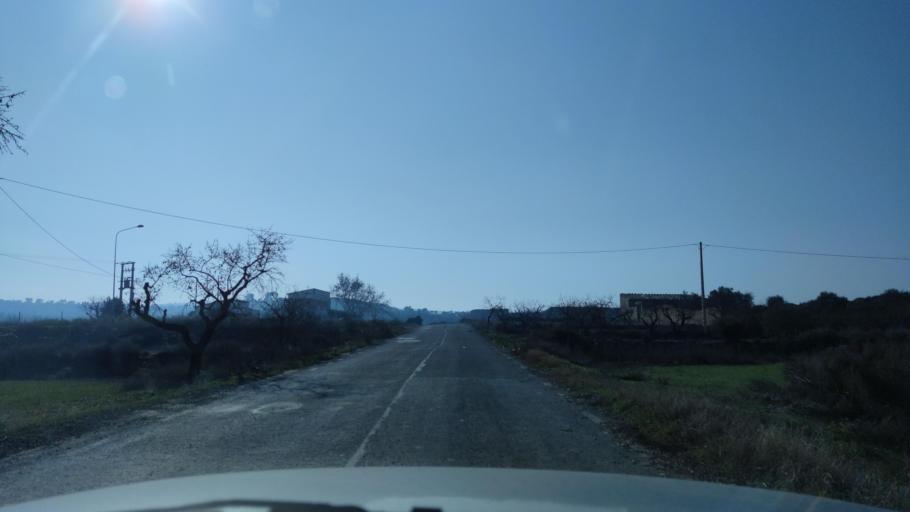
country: ES
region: Catalonia
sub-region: Provincia de Lleida
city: Torrebesses
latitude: 41.4567
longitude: 0.5584
